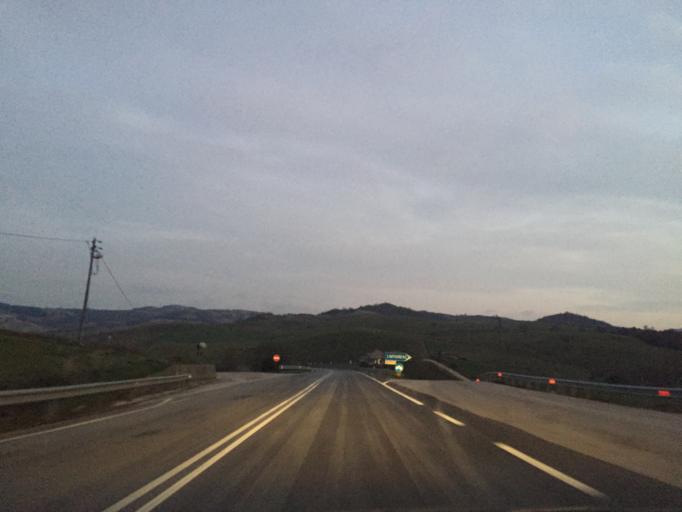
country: IT
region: Apulia
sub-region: Provincia di Foggia
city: Volturara Appula
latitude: 41.4604
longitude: 15.0598
